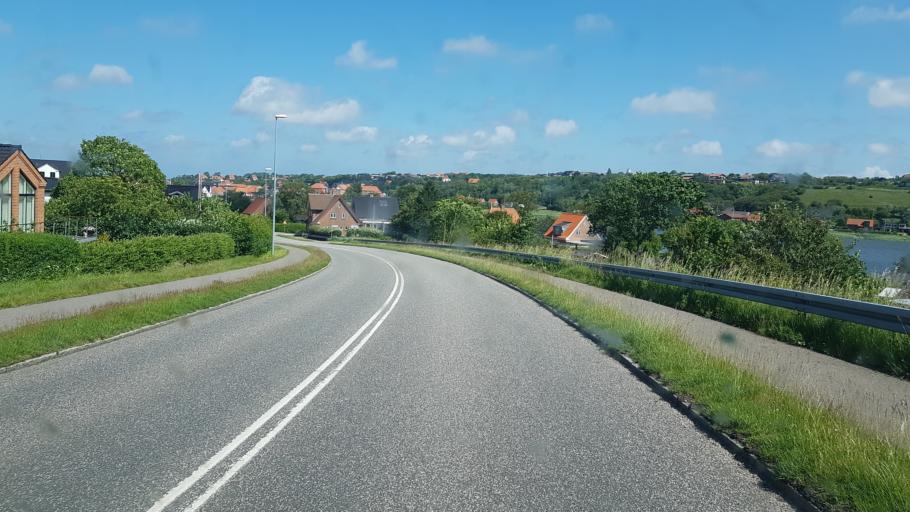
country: DK
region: Central Jutland
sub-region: Lemvig Kommune
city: Lemvig
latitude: 56.5422
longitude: 8.3143
